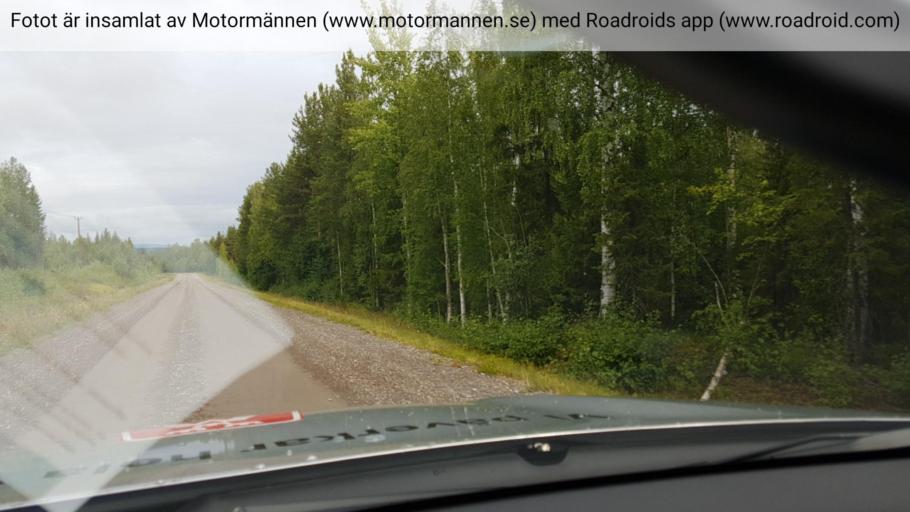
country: SE
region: Norrbotten
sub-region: Alvsbyns Kommun
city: AElvsbyn
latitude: 66.0197
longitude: 21.0332
